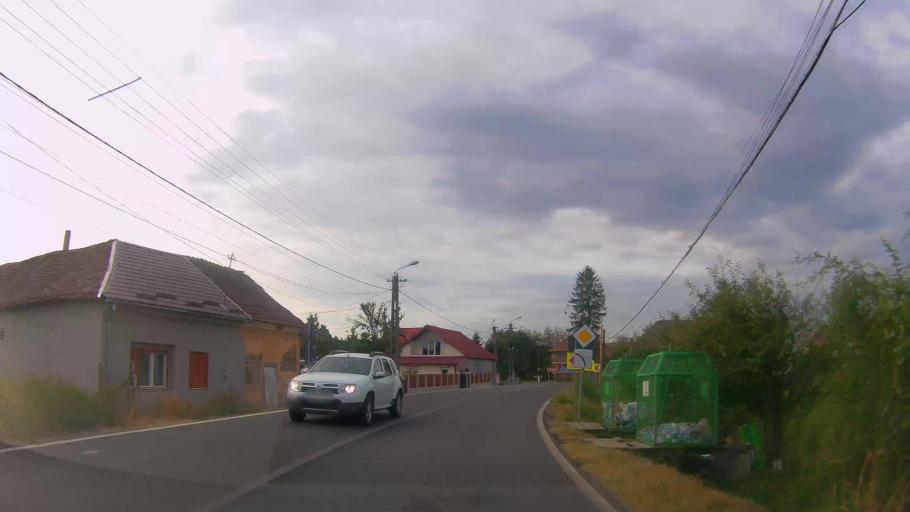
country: RO
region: Satu Mare
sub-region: Comuna Halmeu
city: Halmeu
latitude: 47.9784
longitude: 23.0102
